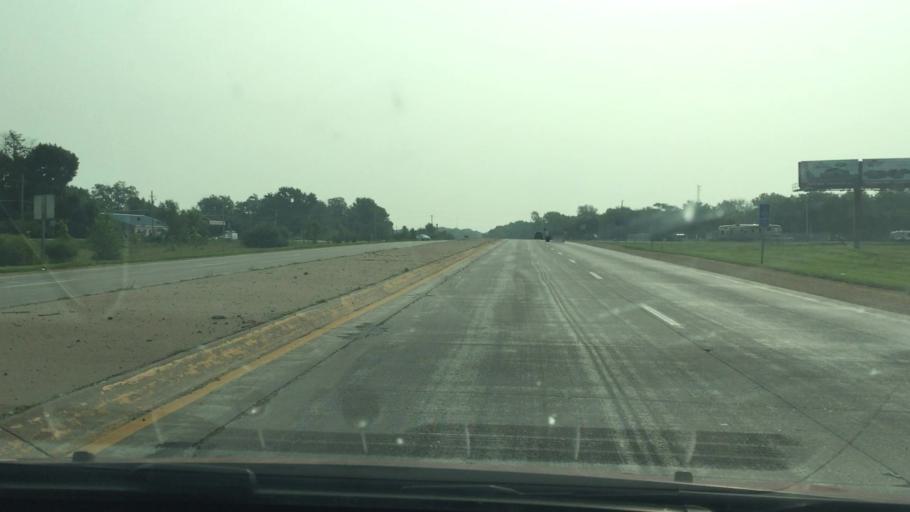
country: US
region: Iowa
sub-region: Scott County
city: Buffalo
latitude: 41.5084
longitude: -90.6868
